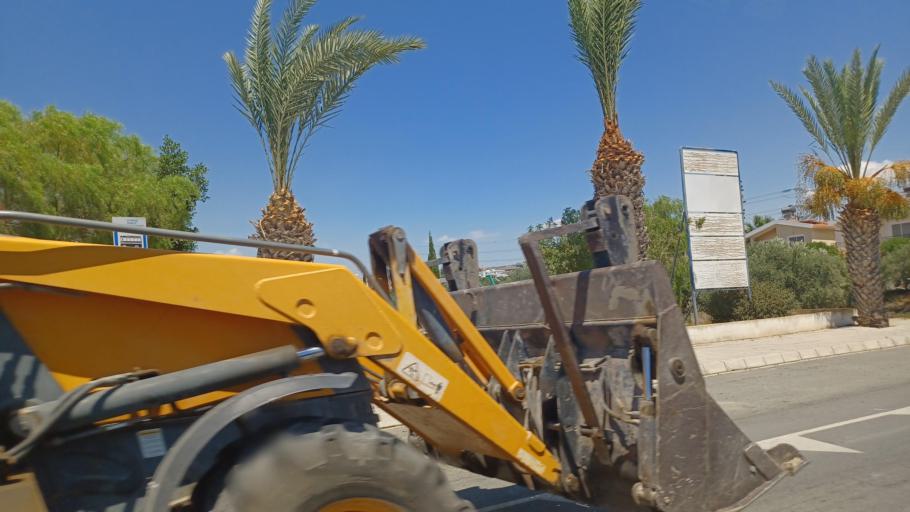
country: CY
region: Larnaka
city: Pyla
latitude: 35.0021
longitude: 33.6882
